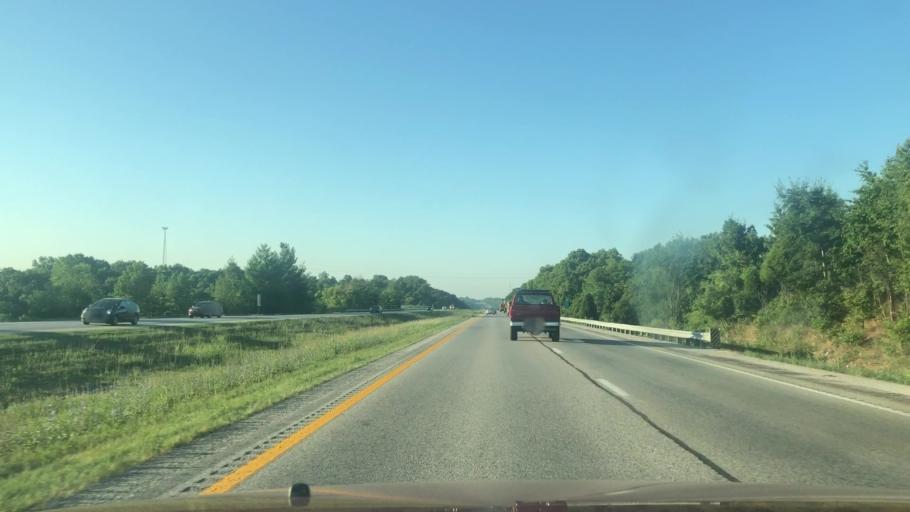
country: US
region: Missouri
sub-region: Christian County
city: Ozark
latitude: 36.8828
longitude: -93.2344
